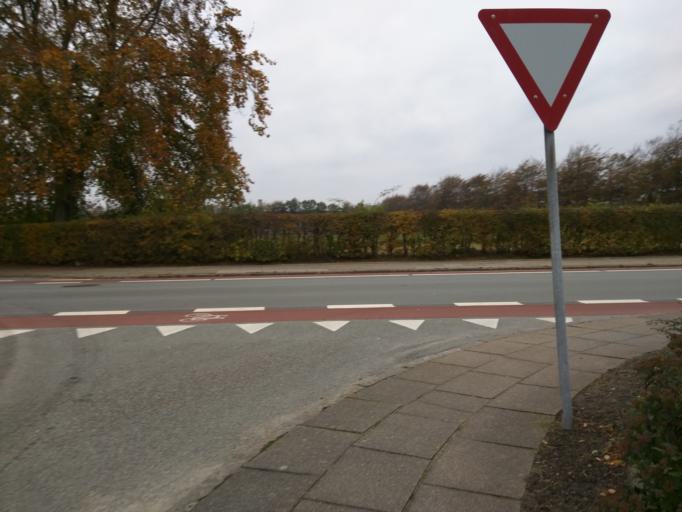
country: DK
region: Central Jutland
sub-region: Viborg Kommune
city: Viborg
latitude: 56.4579
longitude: 9.3888
